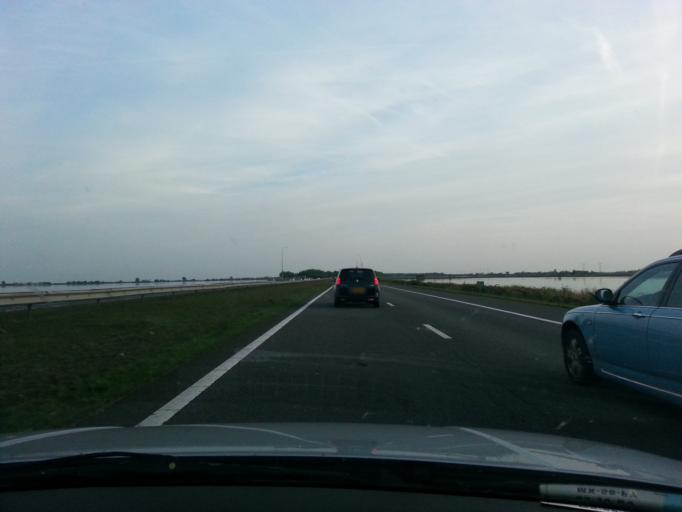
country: NL
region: Friesland
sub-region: Gemeente Skarsterlan
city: Sint Nicolaasga
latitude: 52.9010
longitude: 5.7697
